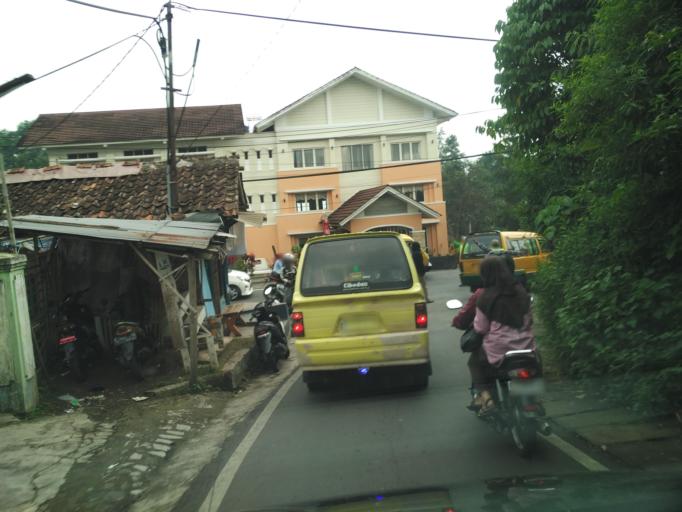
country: ID
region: West Java
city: Caringin
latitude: -6.7258
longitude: 107.0387
